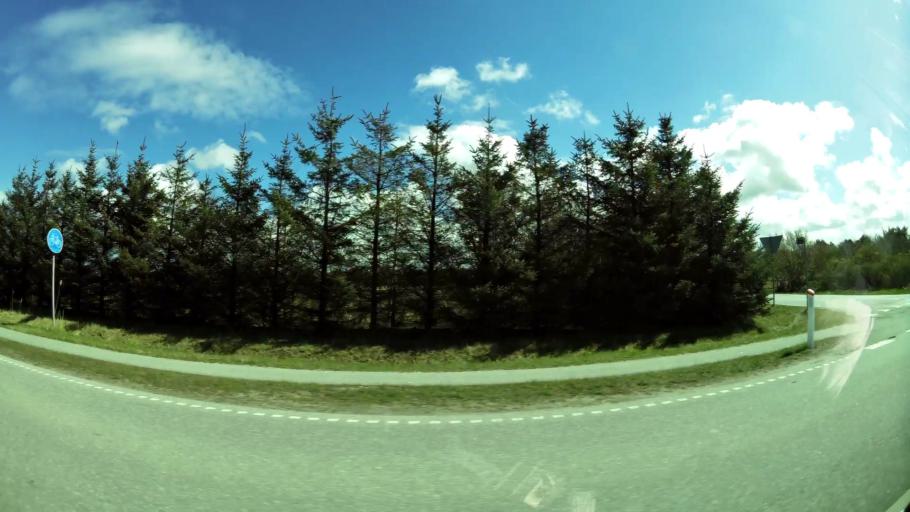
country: DK
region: North Denmark
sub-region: Hjorring Kommune
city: Hirtshals
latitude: 57.5562
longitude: 9.9389
